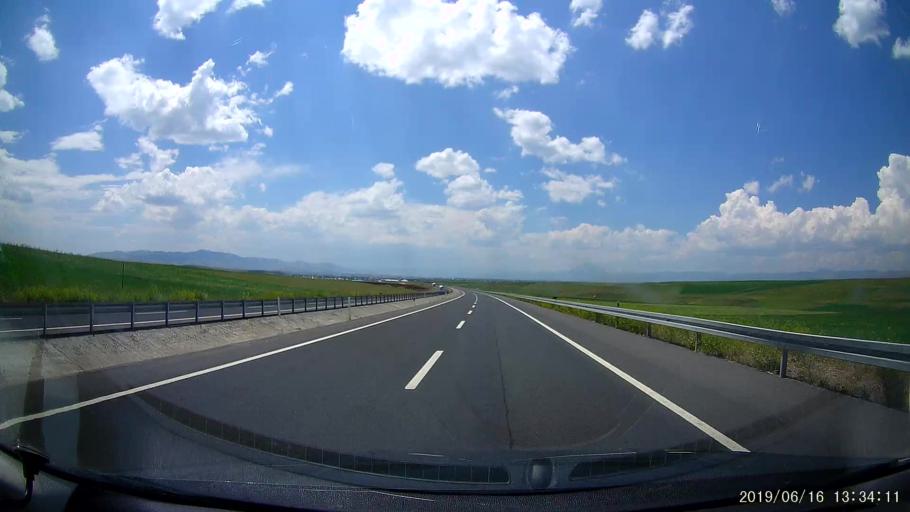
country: TR
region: Agri
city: Agri
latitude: 39.7118
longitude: 43.1335
